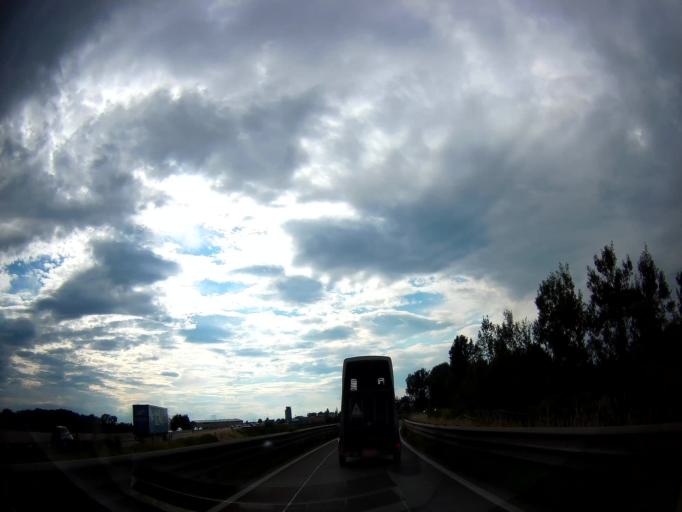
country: AT
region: Lower Austria
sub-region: Politischer Bezirk Korneuburg
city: Stockerau
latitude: 48.3823
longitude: 16.1904
